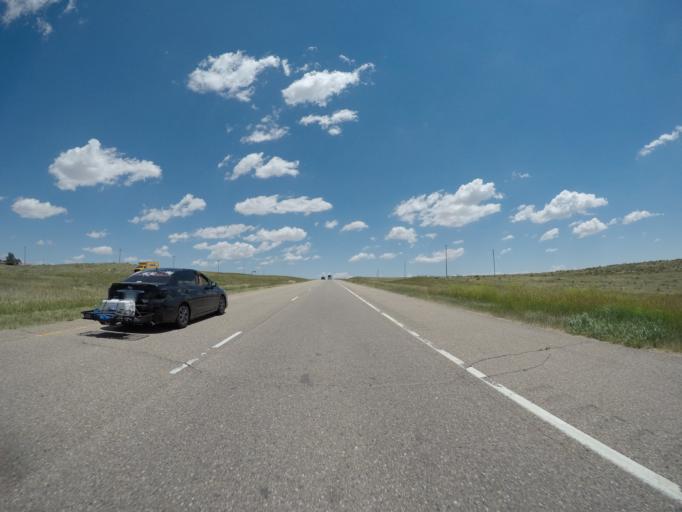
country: US
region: Colorado
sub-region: Lincoln County
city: Hugo
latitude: 39.2716
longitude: -103.5112
